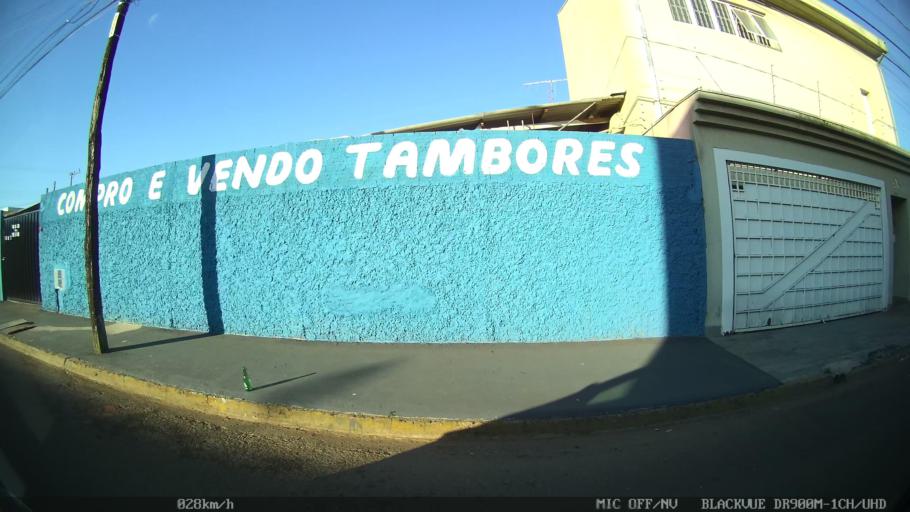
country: BR
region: Sao Paulo
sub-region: Franca
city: Franca
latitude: -20.5254
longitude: -47.3725
